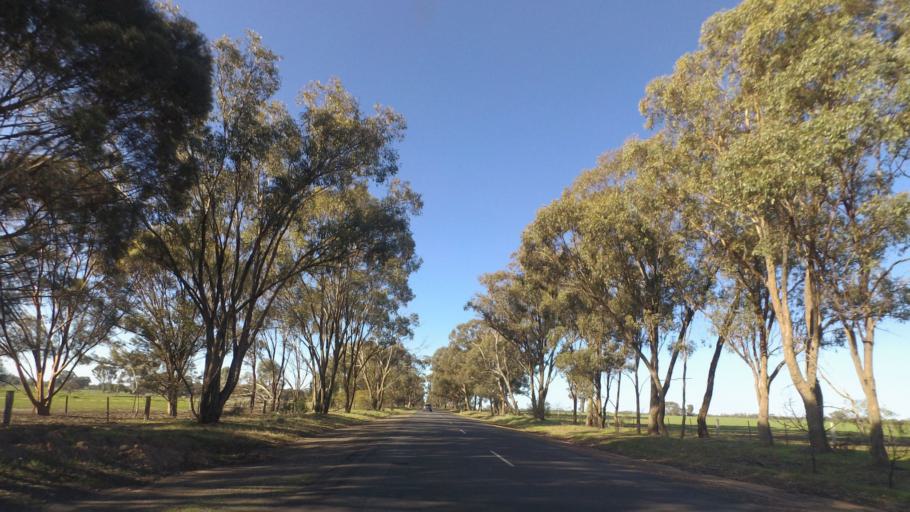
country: AU
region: Victoria
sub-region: Greater Bendigo
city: Epsom
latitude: -36.6592
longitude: 144.4718
